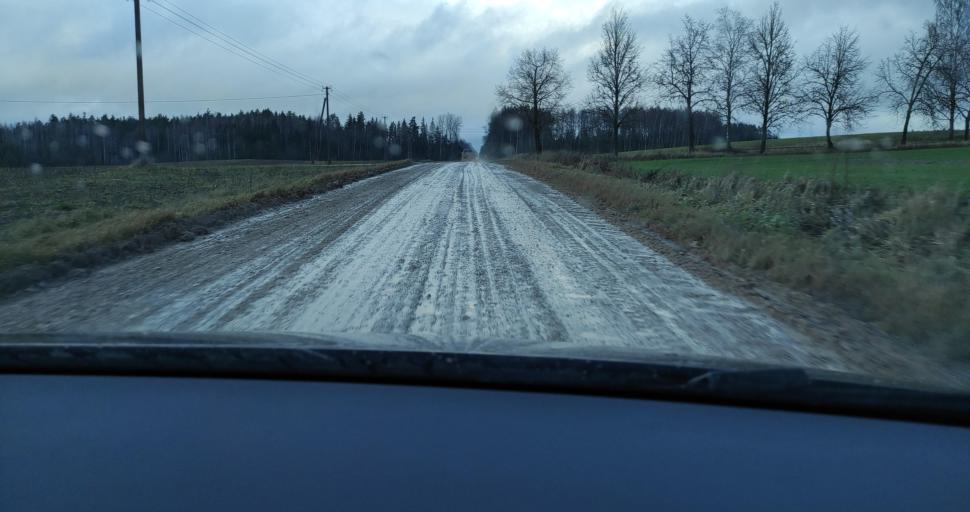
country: LV
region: Skrunda
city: Skrunda
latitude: 56.7166
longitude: 22.2015
